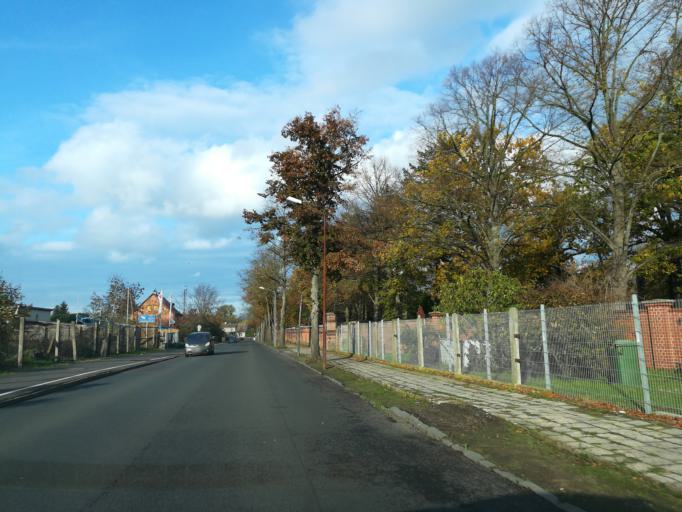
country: DE
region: Saxony-Anhalt
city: Haldensleben I
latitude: 52.2837
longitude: 11.4221
